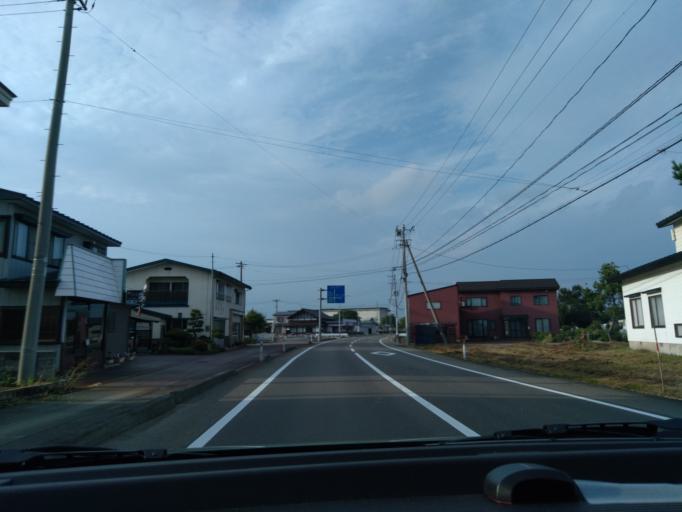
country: JP
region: Akita
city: Yokotemachi
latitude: 39.3845
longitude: 140.5306
